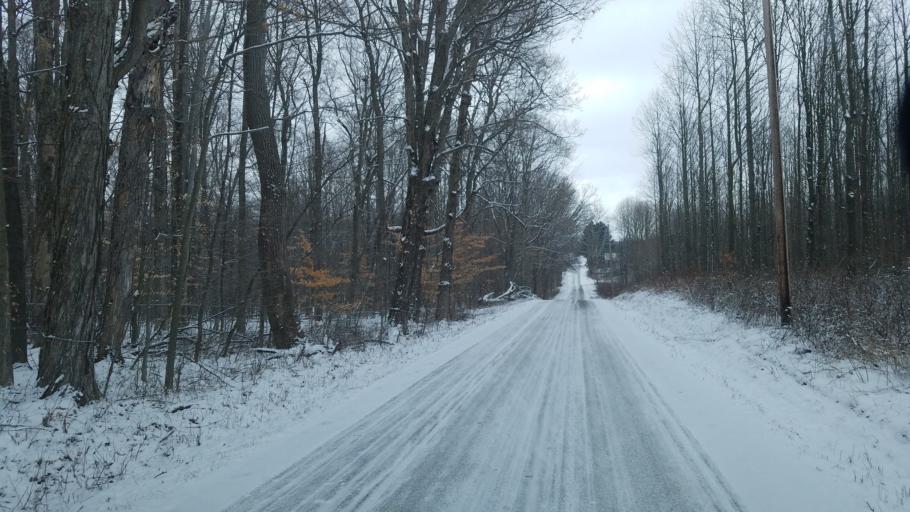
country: US
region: Ohio
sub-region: Knox County
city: Fredericktown
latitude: 40.5427
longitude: -82.5789
